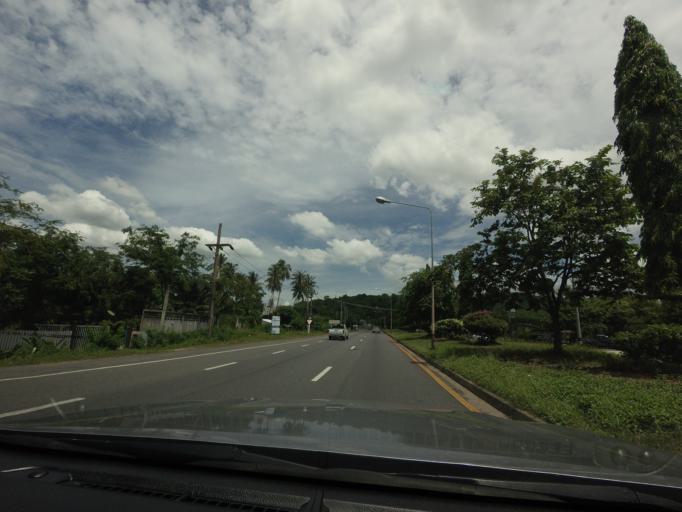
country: TH
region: Songkhla
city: Ban Mai
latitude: 7.1676
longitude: 100.5478
